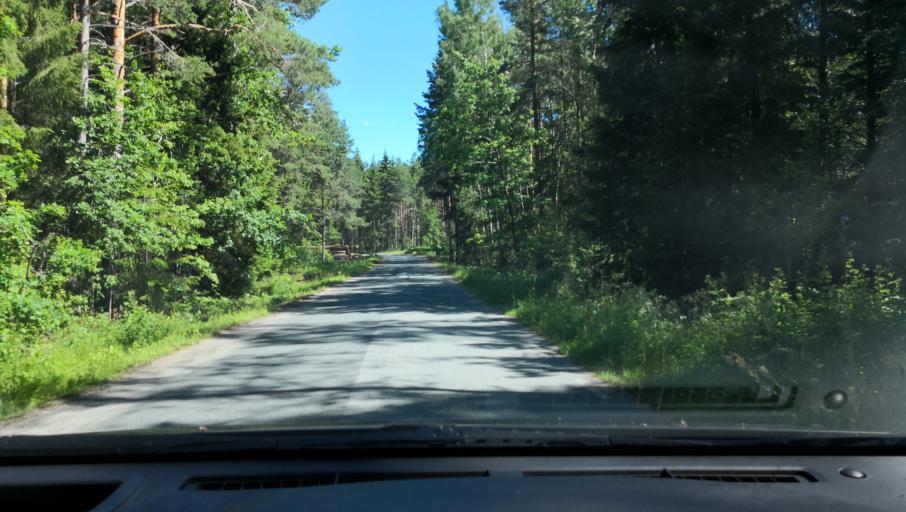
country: SE
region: Soedermanland
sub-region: Eskilstuna Kommun
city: Hallbybrunn
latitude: 59.3042
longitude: 16.3732
